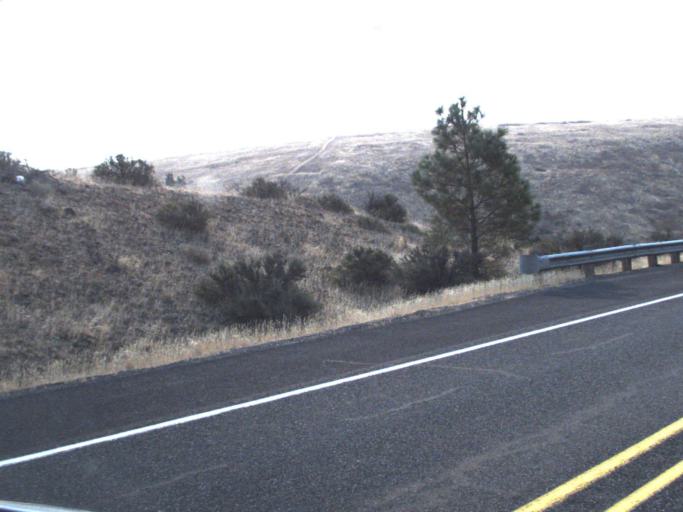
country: US
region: Washington
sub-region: Kittitas County
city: Ellensburg
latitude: 47.1451
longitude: -120.6922
